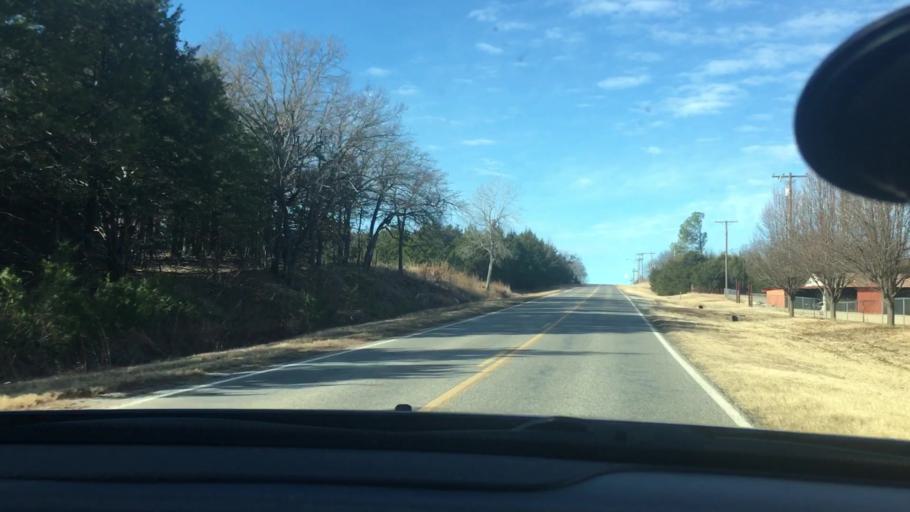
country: US
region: Oklahoma
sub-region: Seminole County
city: Konawa
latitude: 34.9859
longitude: -96.9160
